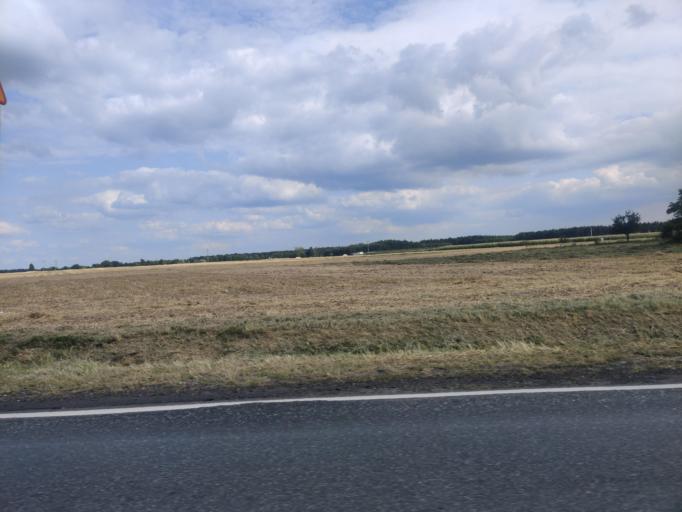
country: PL
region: Greater Poland Voivodeship
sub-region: Powiat koninski
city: Stare Miasto
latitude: 52.1452
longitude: 18.1969
